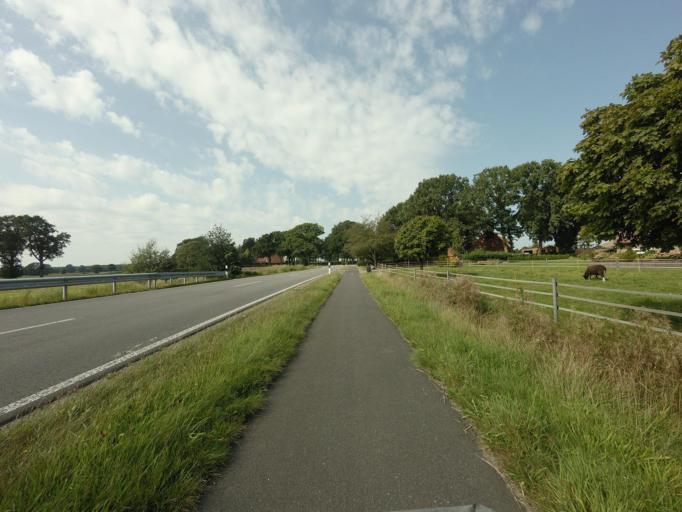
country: DE
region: Lower Saxony
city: Wielen
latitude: 52.5361
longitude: 6.7599
